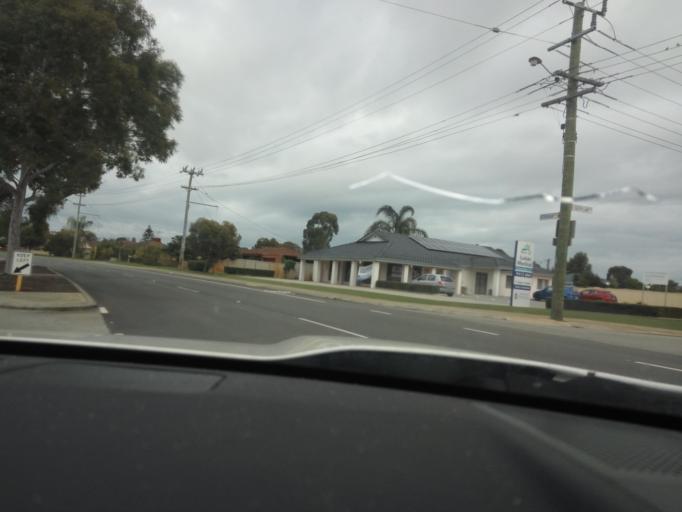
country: AU
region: Western Australia
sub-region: City of Cockburn
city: South Lake
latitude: -32.1118
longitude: 115.8388
